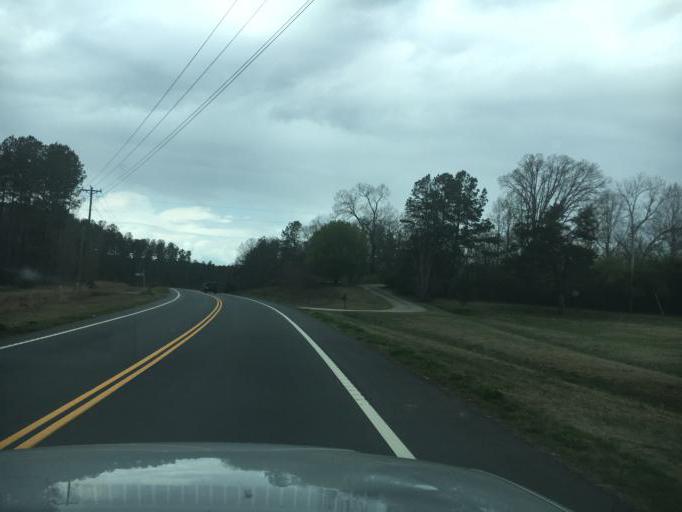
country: US
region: South Carolina
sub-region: Oconee County
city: Walhalla
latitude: 34.8085
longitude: -83.0323
